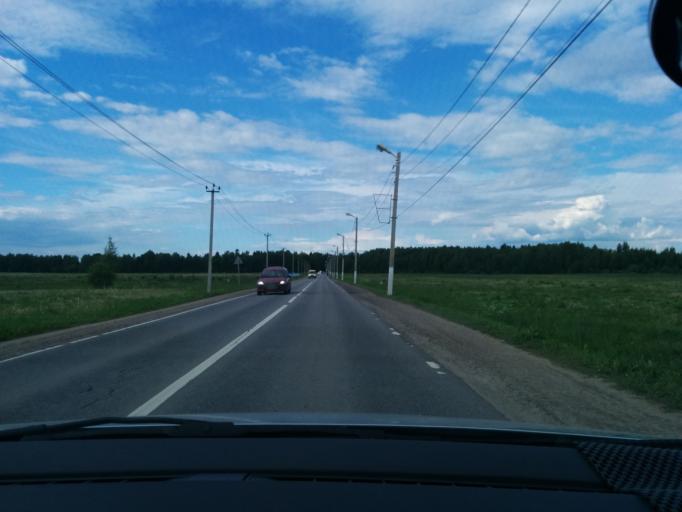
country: RU
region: Moskovskaya
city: Lugovaya
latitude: 56.0307
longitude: 37.4655
